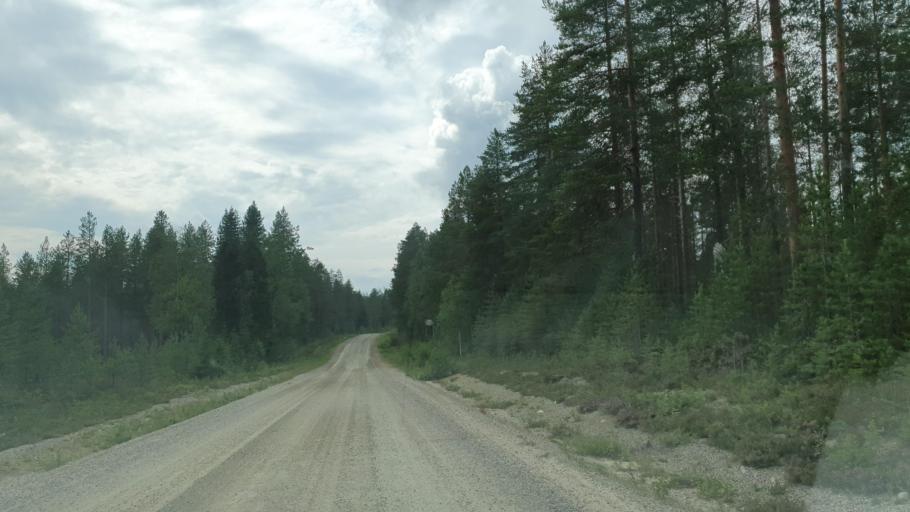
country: FI
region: Kainuu
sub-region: Kehys-Kainuu
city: Kuhmo
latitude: 64.7288
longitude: 29.7165
